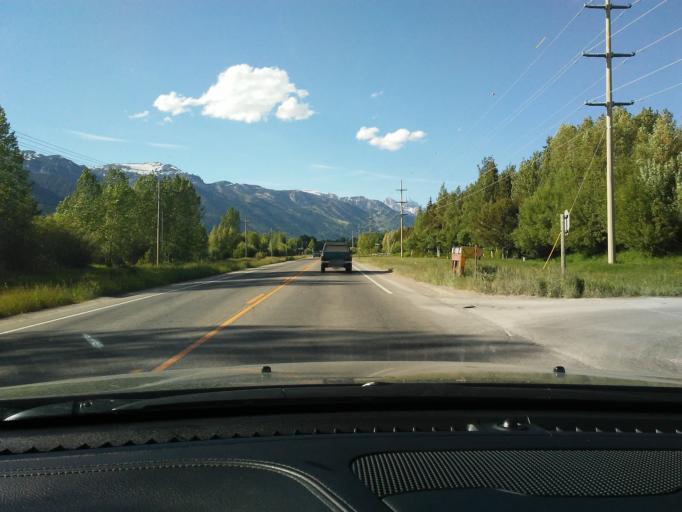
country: US
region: Wyoming
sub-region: Teton County
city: Moose Wilson Road
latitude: 43.5249
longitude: -110.8421
